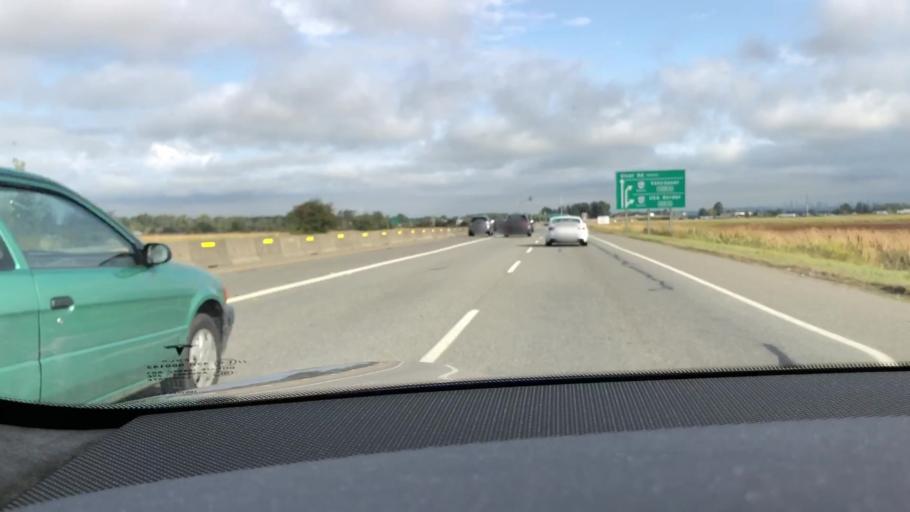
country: CA
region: British Columbia
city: Ladner
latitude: 49.0974
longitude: -123.0580
